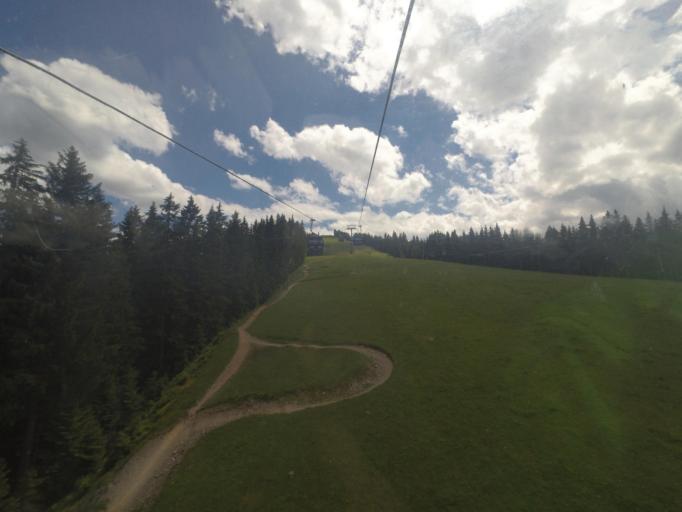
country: AT
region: Salzburg
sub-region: Politischer Bezirk Zell am See
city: Leogang
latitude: 47.4208
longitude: 12.7142
